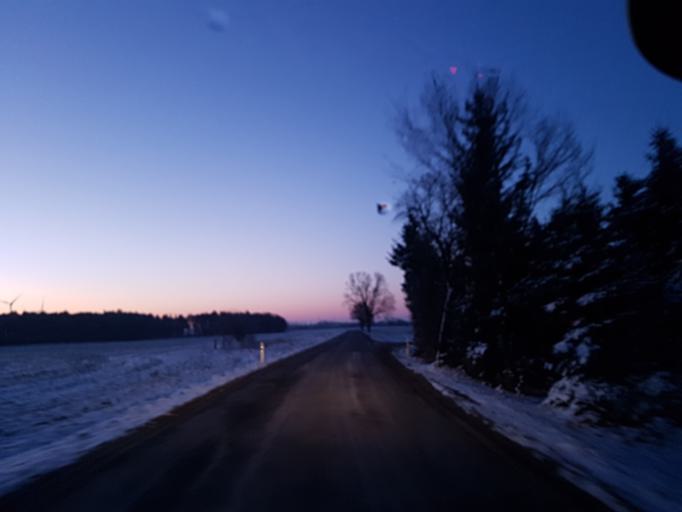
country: DE
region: Brandenburg
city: Falkenberg
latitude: 51.5278
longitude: 13.2987
